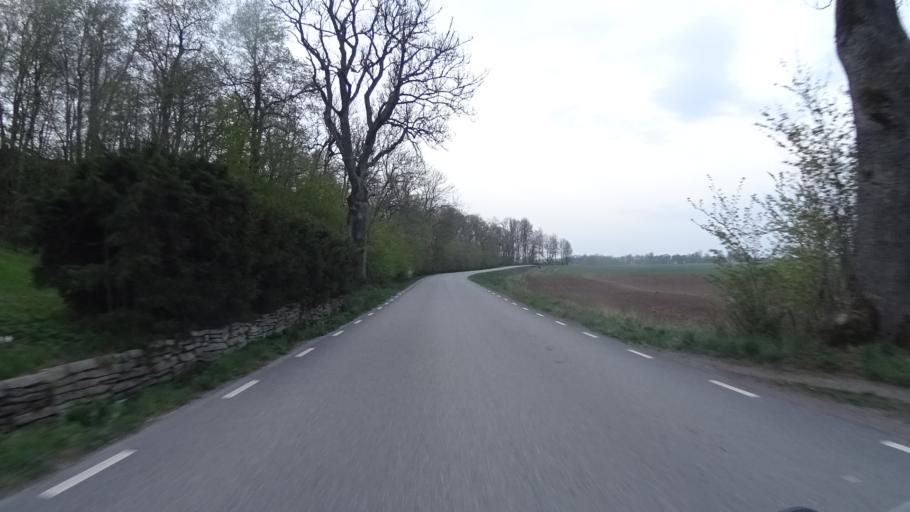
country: SE
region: Vaestra Goetaland
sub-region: Gotene Kommun
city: Kallby
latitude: 58.5543
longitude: 13.3464
